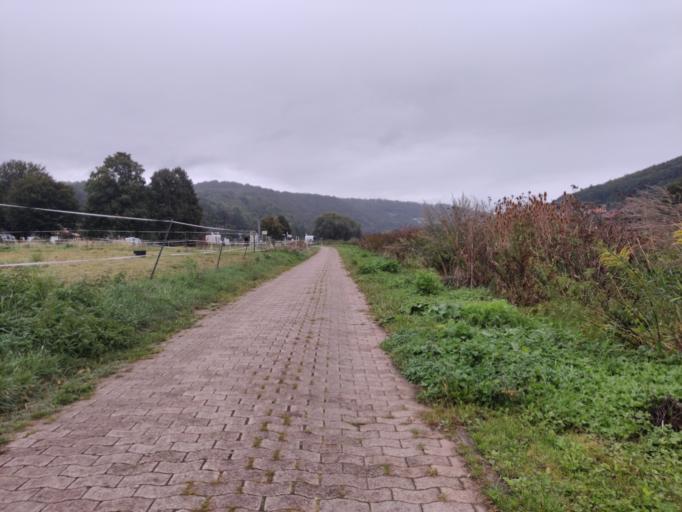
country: DE
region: Lower Saxony
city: Bad Karlshafen
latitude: 51.6438
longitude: 9.4166
